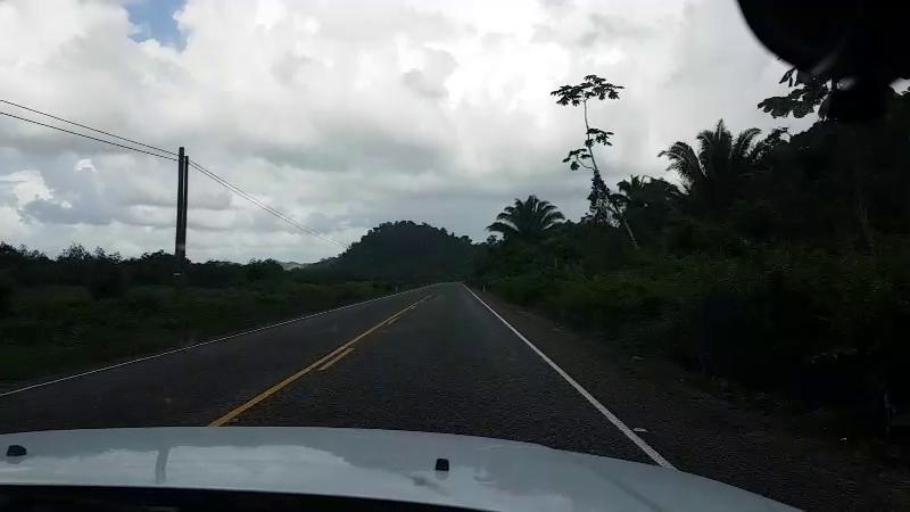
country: BZ
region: Cayo
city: Belmopan
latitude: 17.1517
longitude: -88.6936
